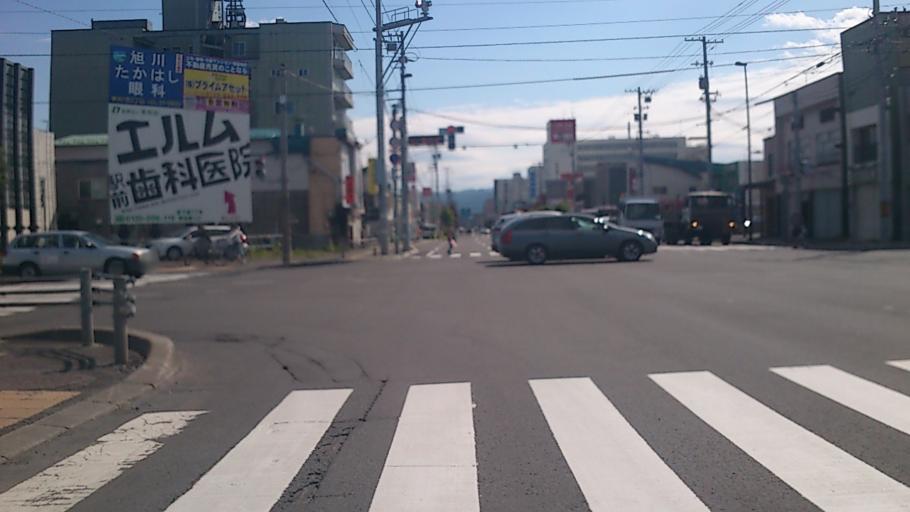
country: JP
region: Hokkaido
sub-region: Asahikawa-shi
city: Asahikawa
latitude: 43.7865
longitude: 142.3633
